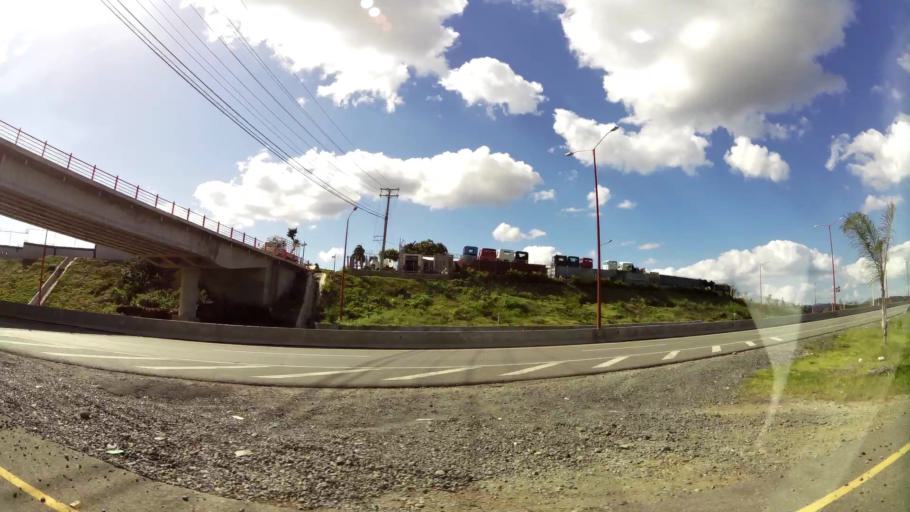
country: DO
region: Santo Domingo
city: Santo Domingo Oeste
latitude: 18.5605
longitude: -70.0696
